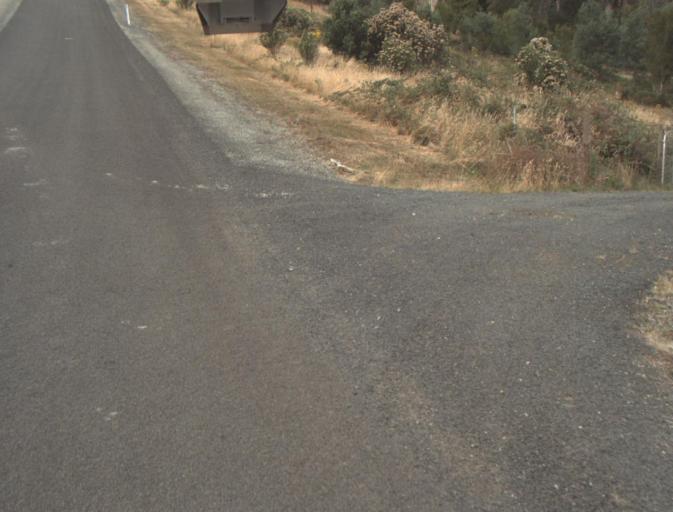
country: AU
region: Tasmania
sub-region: Launceston
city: Mayfield
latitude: -41.3013
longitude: 147.0426
